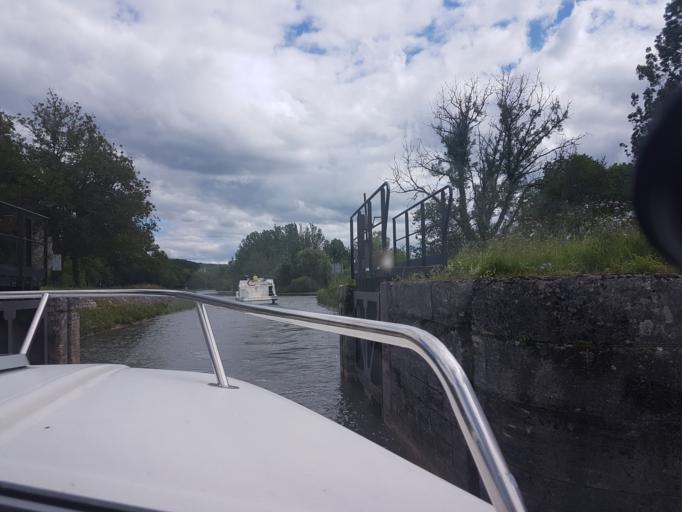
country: FR
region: Bourgogne
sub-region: Departement de l'Yonne
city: Vermenton
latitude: 47.5856
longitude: 3.6419
